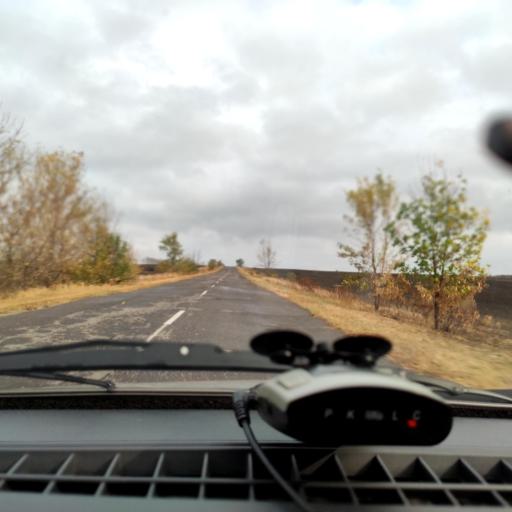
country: RU
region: Voronezj
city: Uryv-Pokrovka
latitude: 51.2362
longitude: 38.9434
